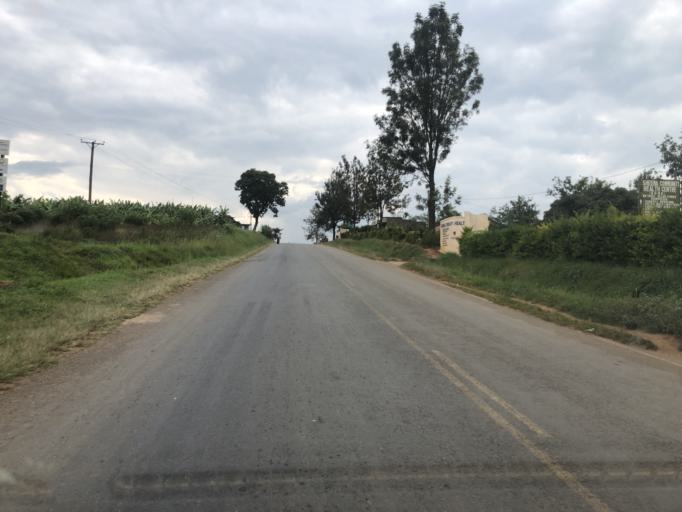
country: UG
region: Western Region
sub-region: Sheema District
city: Kibingo
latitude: -0.5789
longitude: 30.4094
